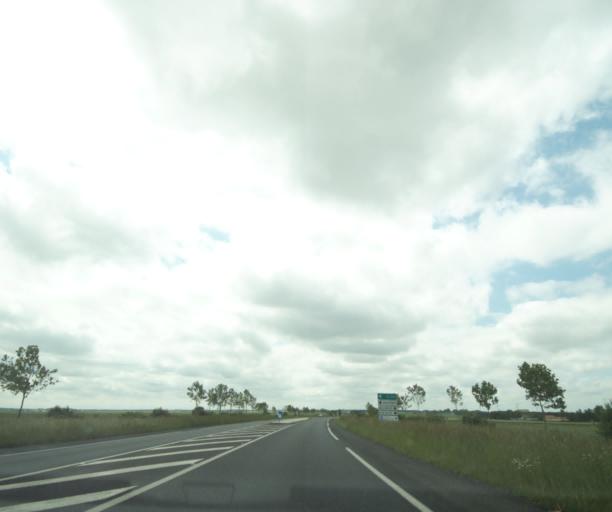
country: FR
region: Poitou-Charentes
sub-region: Departement des Deux-Sevres
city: Saint-Varent
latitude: 46.9035
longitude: -0.1910
